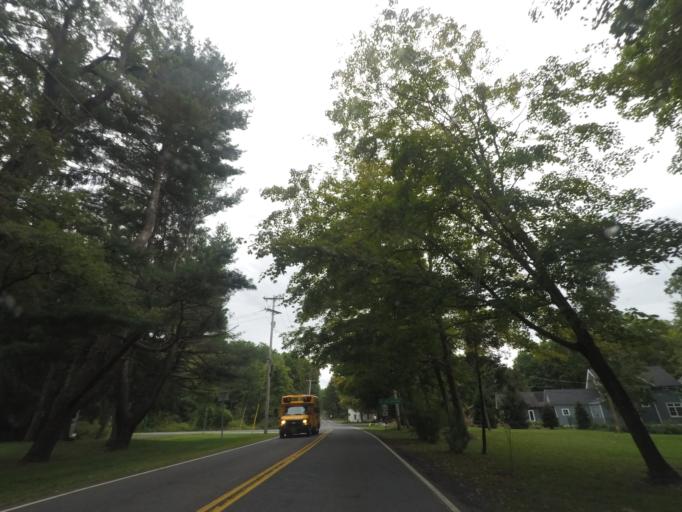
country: US
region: New York
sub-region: Rensselaer County
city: Nassau
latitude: 42.4688
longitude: -73.5819
